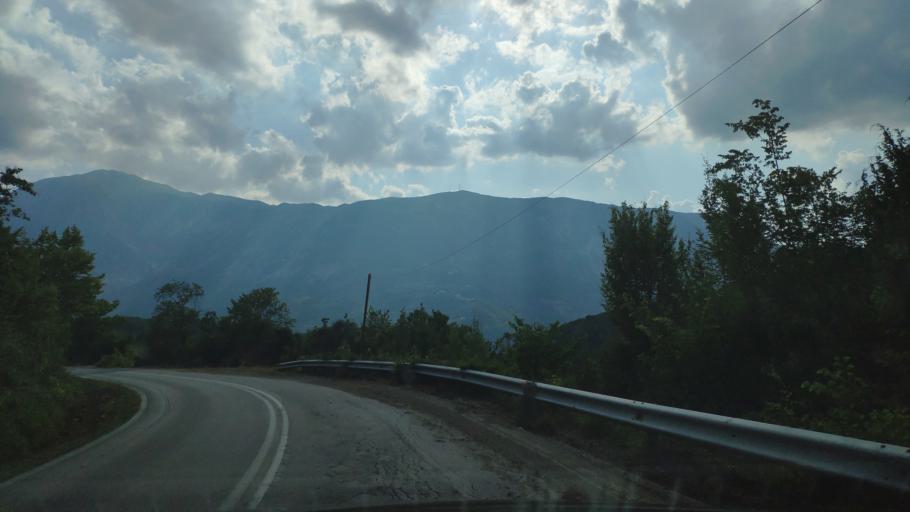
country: GR
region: Epirus
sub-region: Nomos Artas
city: Agios Dimitrios
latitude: 39.4596
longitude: 21.0593
